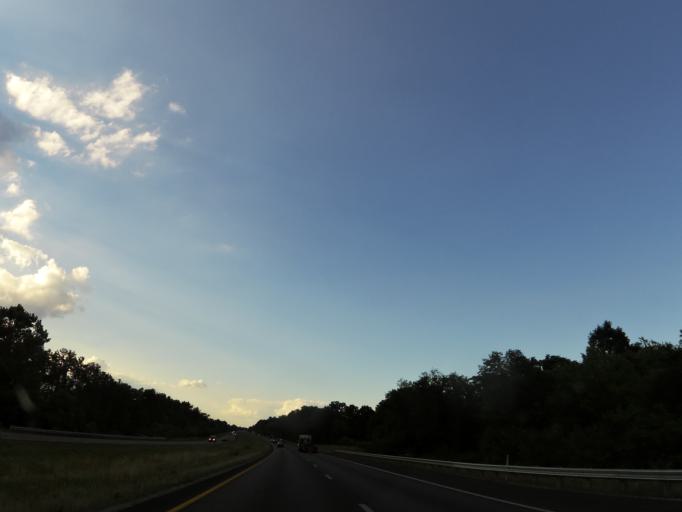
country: US
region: Tennessee
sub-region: Williamson County
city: Thompson's Station
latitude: 35.7629
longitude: -86.8653
